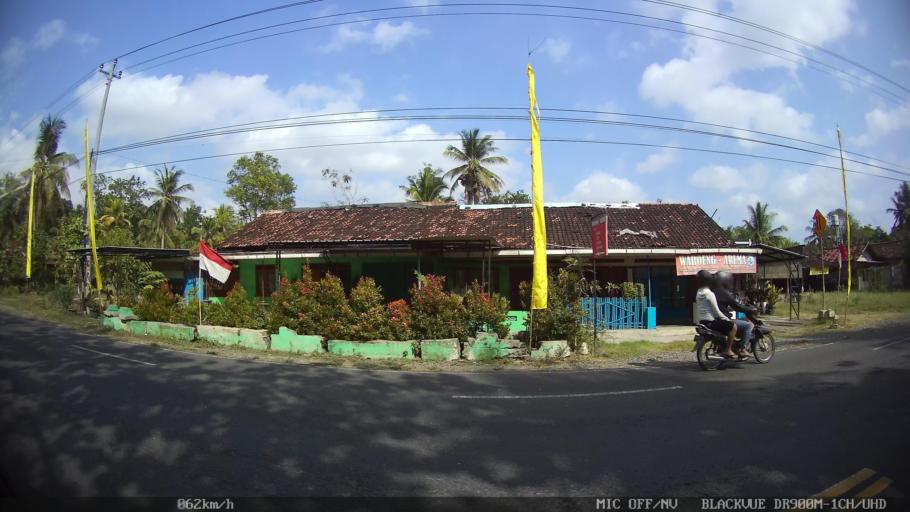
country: ID
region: Daerah Istimewa Yogyakarta
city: Srandakan
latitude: -7.8603
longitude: 110.2119
